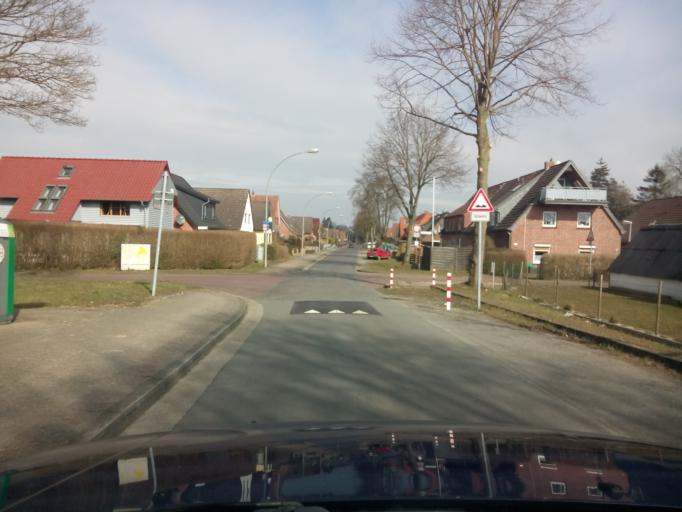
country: DE
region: Lower Saxony
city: Ritterhude
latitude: 53.1883
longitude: 8.7606
